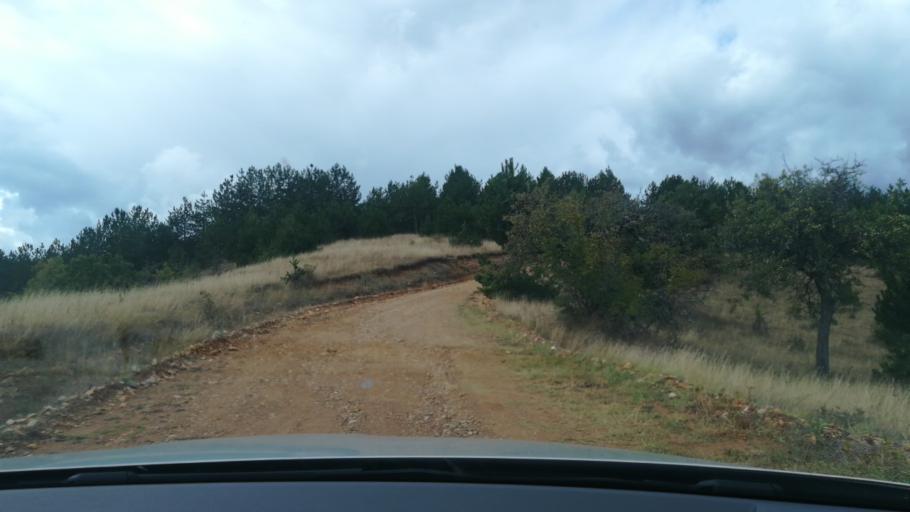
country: MK
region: Makedonska Kamenica
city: Makedonska Kamenica
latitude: 42.0066
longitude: 22.6063
